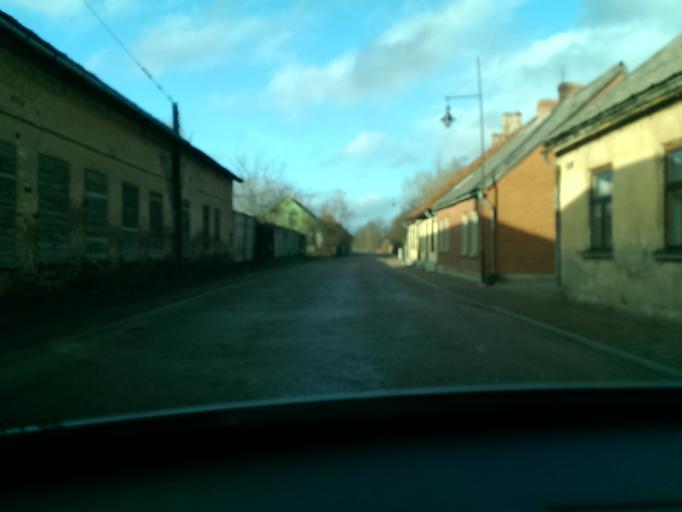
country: LV
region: Kuldigas Rajons
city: Kuldiga
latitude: 56.9727
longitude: 21.9706
